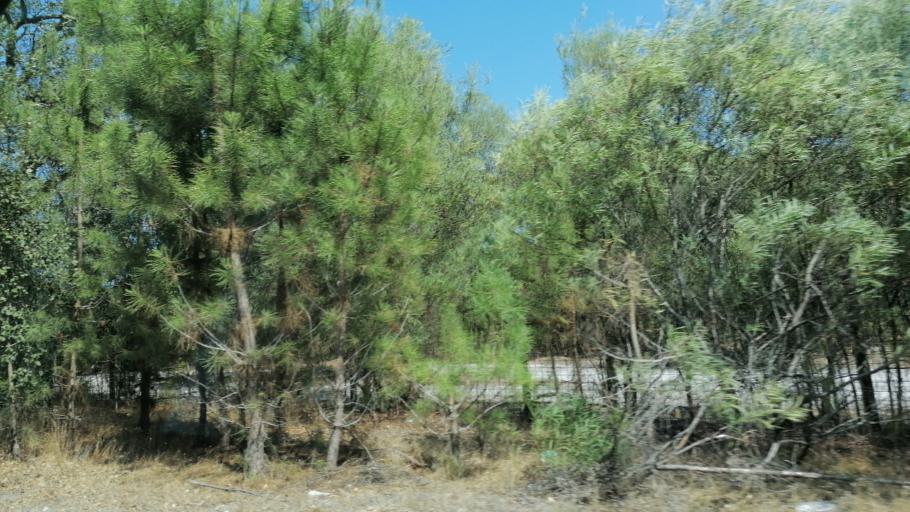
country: PT
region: Santarem
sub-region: Benavente
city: Poceirao
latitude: 38.7268
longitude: -8.7046
